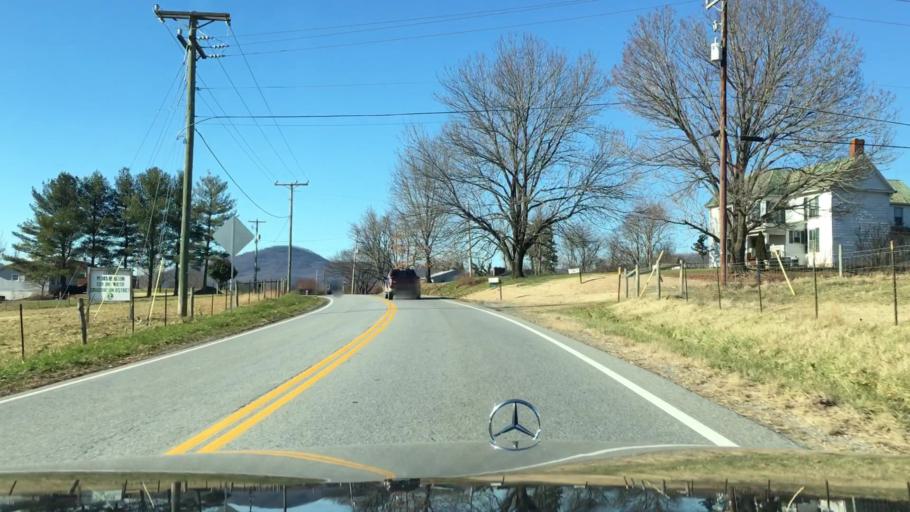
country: US
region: Virginia
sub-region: Botetourt County
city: Blue Ridge
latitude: 37.2675
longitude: -79.7594
